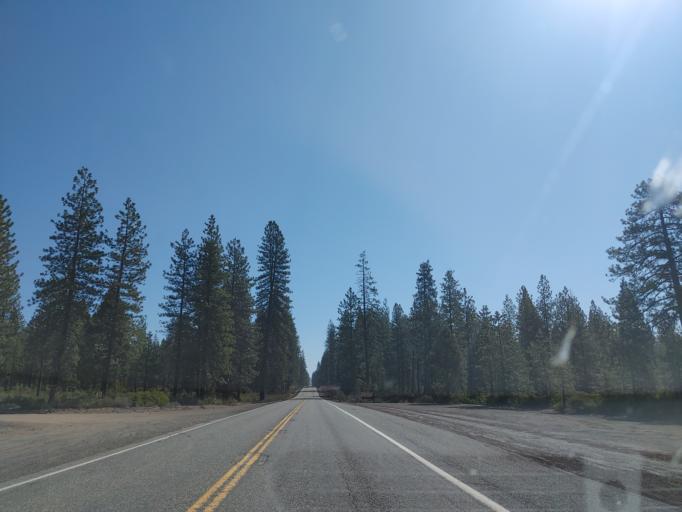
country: US
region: California
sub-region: Siskiyou County
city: McCloud
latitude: 41.2562
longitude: -122.0406
